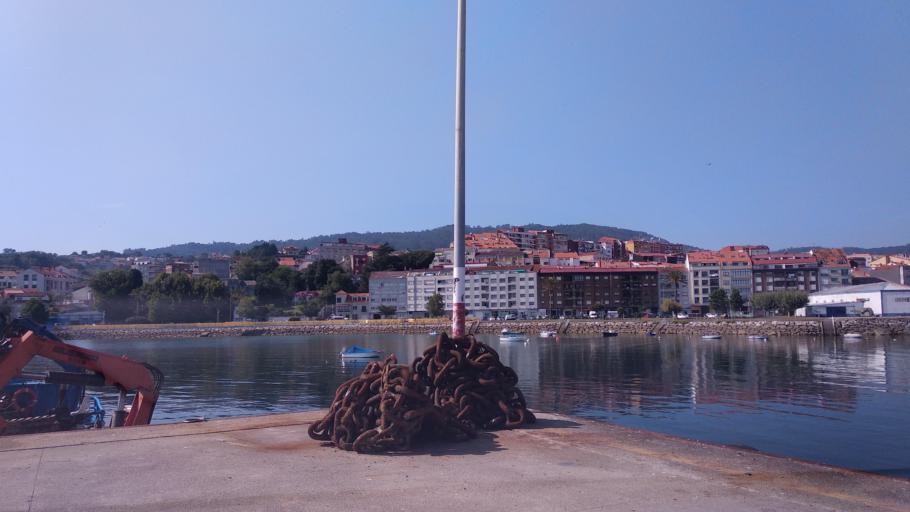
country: ES
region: Galicia
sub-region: Provincia de Pontevedra
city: Moana
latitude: 42.2720
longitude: -8.7369
